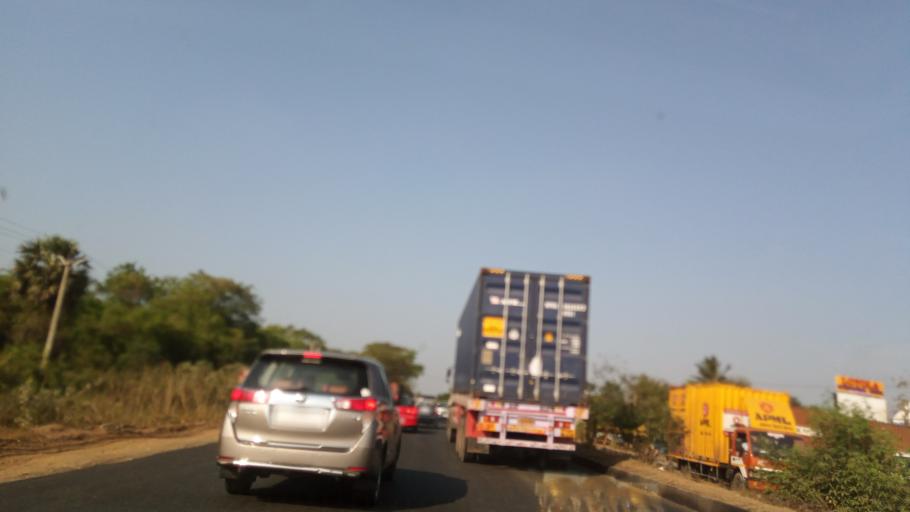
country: IN
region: Tamil Nadu
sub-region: Kancheepuram
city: Nandambakkam
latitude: 13.0261
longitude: 80.0263
